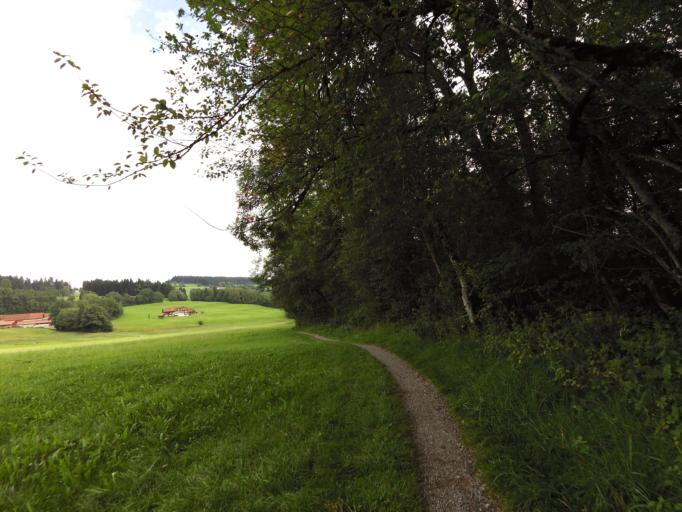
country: DE
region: Bavaria
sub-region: Swabia
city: Weiler-Simmerberg
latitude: 47.5781
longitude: 9.9049
